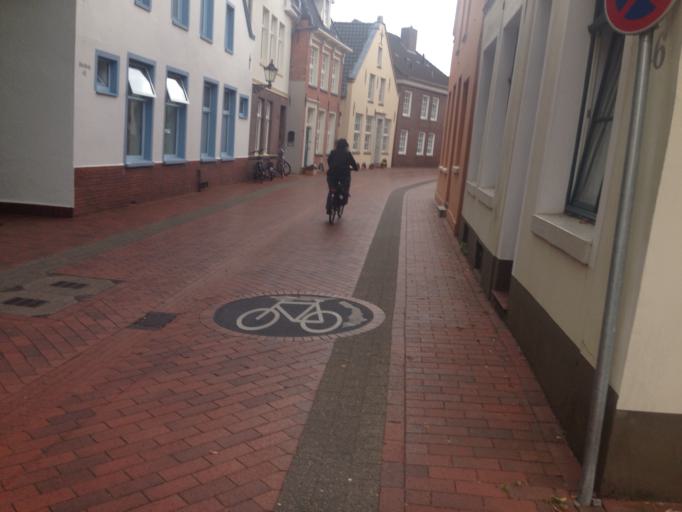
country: DE
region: Lower Saxony
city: Leer
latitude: 53.2246
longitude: 7.4487
